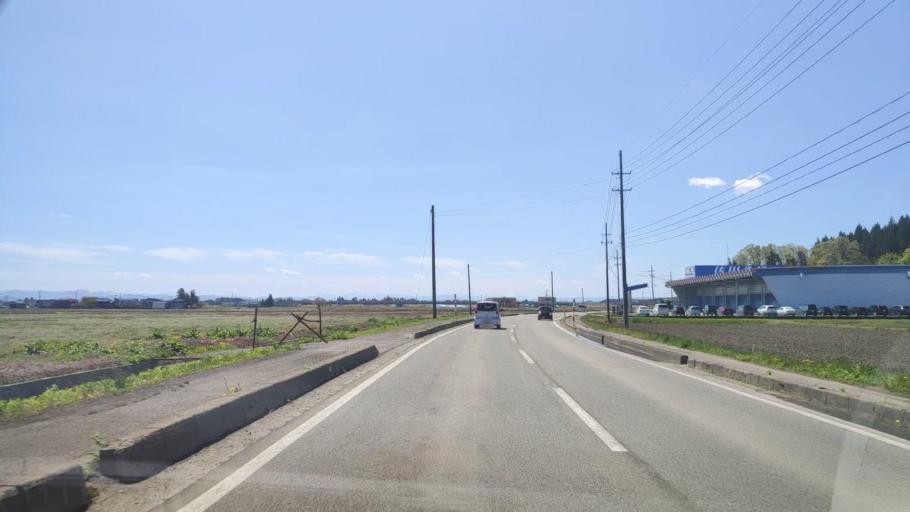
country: JP
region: Akita
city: Omagari
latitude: 39.4417
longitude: 140.4485
